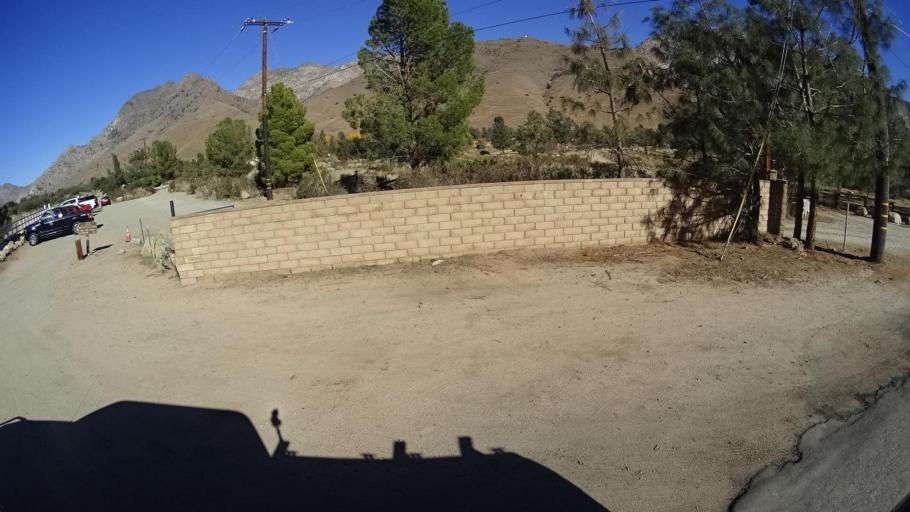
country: US
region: California
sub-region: Kern County
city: Kernville
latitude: 35.7760
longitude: -118.4452
